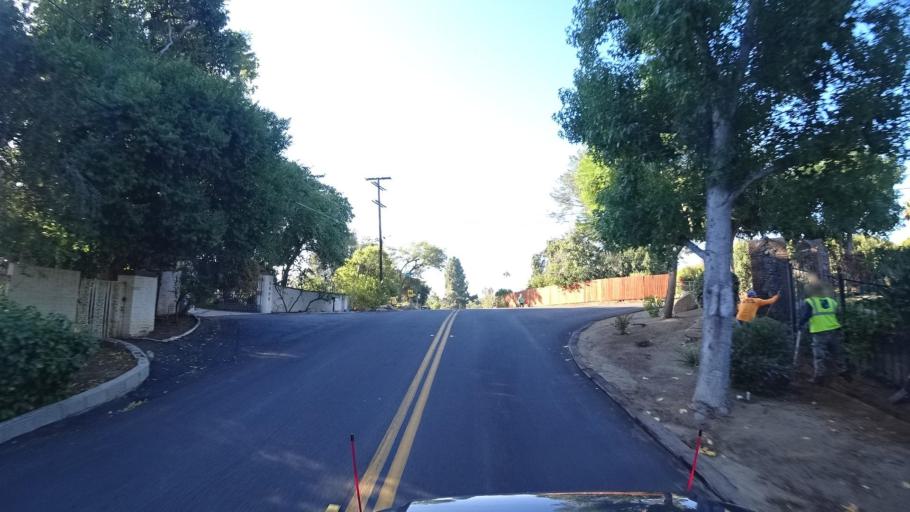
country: US
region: California
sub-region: San Diego County
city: Casa de Oro-Mount Helix
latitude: 32.7706
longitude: -116.9659
